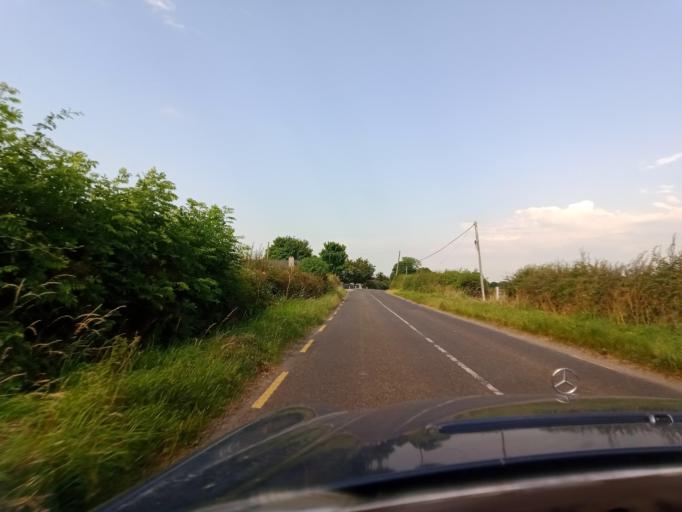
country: IE
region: Leinster
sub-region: Kilkenny
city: Callan
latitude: 52.5157
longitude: -7.3100
